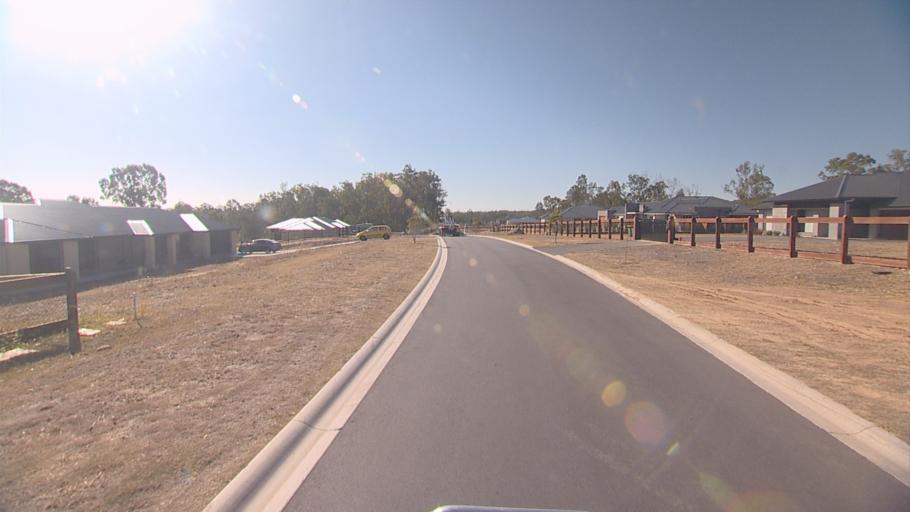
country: AU
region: Queensland
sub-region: Logan
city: Cedar Vale
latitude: -27.8684
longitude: 153.0529
